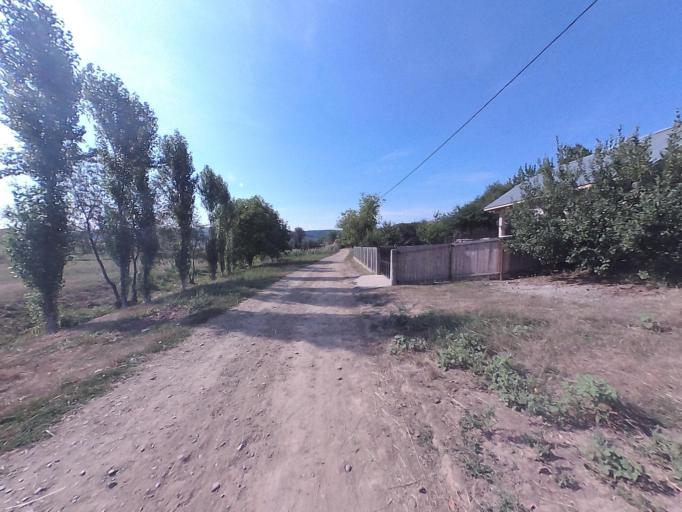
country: RO
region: Vaslui
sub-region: Comuna Osesti
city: Buda
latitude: 46.7663
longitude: 27.4303
